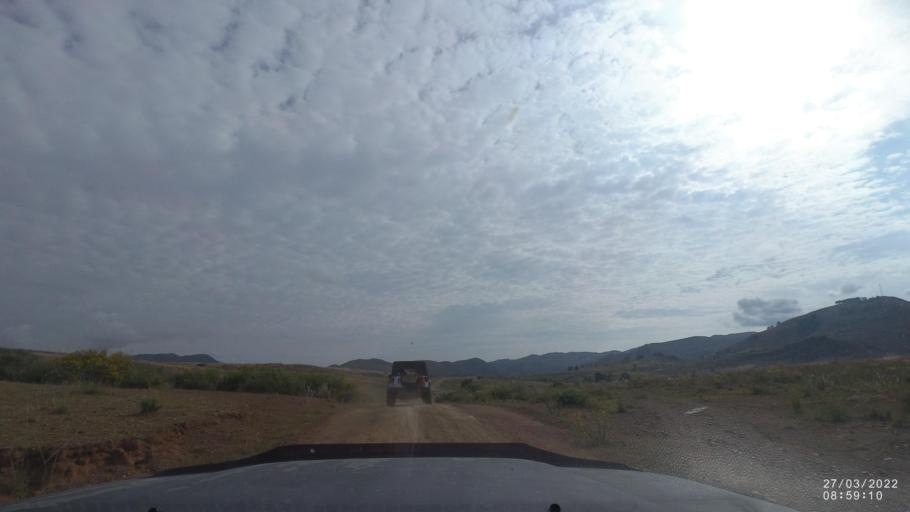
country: BO
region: Cochabamba
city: Cliza
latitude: -17.7403
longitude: -65.8551
